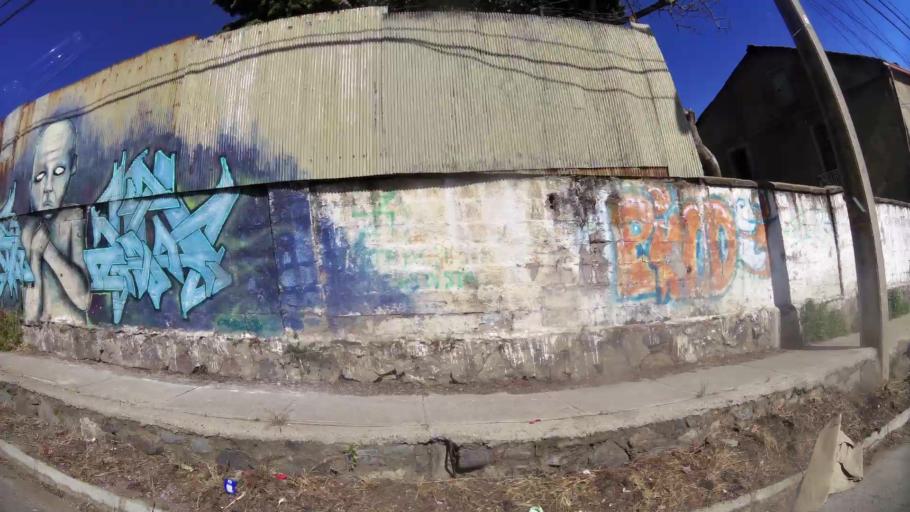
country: CL
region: Valparaiso
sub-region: Provincia de Valparaiso
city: Valparaiso
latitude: -33.0616
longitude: -71.5934
